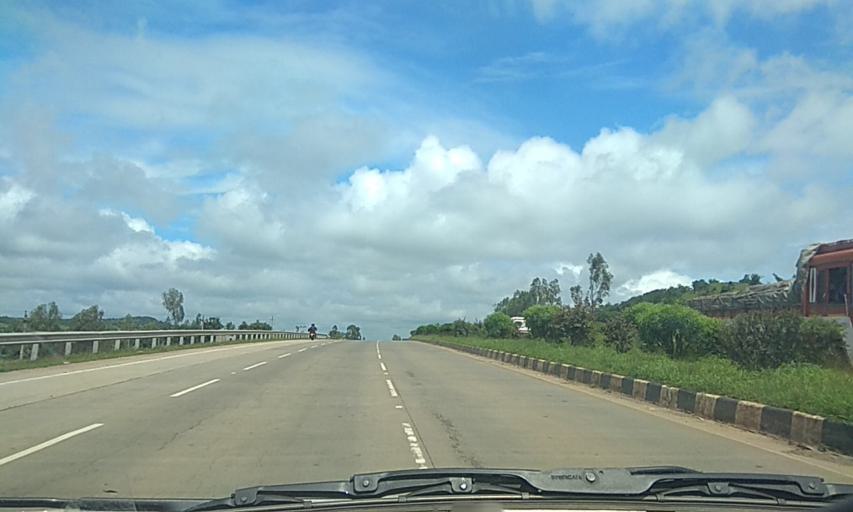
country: IN
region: Karnataka
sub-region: Dharwad
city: Alnavar
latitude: 15.6143
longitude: 74.7634
